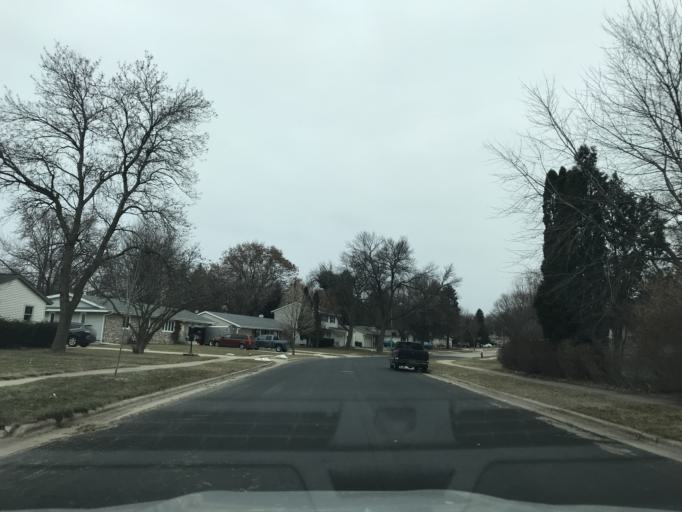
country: US
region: Wisconsin
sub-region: Dane County
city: Monona
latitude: 43.0881
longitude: -89.3045
